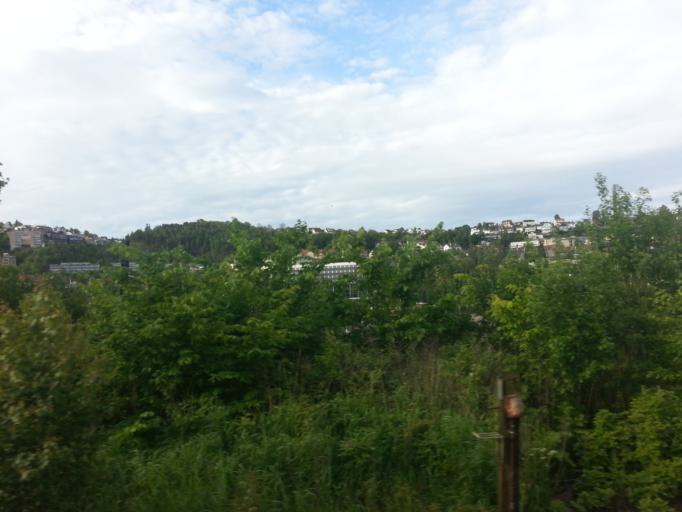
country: NO
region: Oslo
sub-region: Oslo
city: Oslo
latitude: 59.9059
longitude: 10.7829
